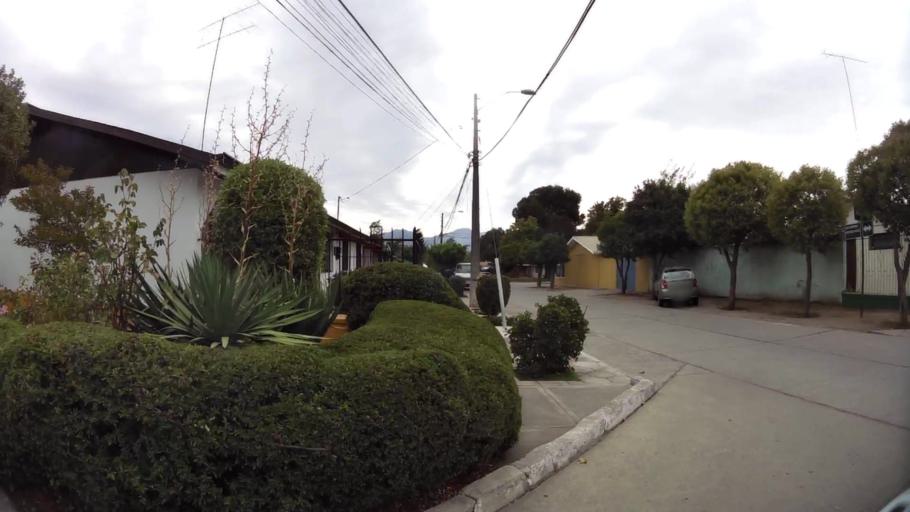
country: CL
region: O'Higgins
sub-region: Provincia de Cachapoal
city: Rancagua
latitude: -34.1564
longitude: -70.7389
